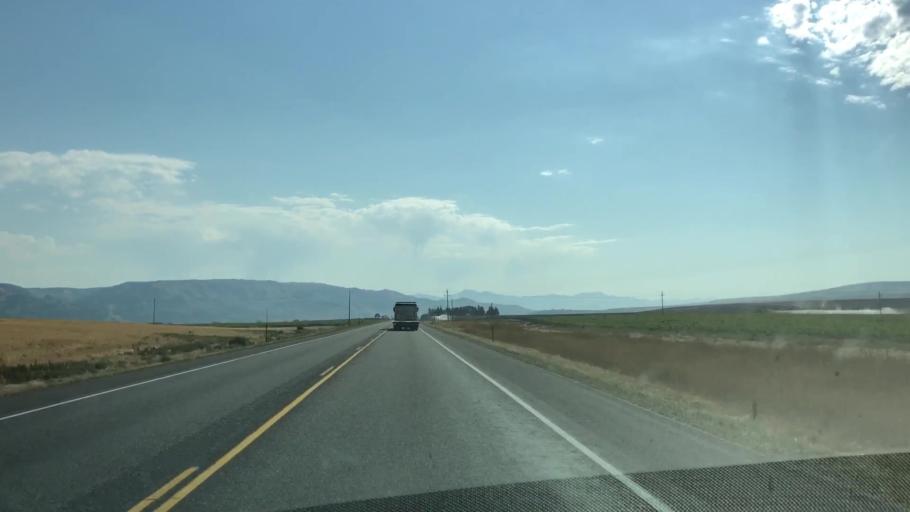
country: US
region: Idaho
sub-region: Jefferson County
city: Rigby
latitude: 43.6143
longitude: -111.7508
